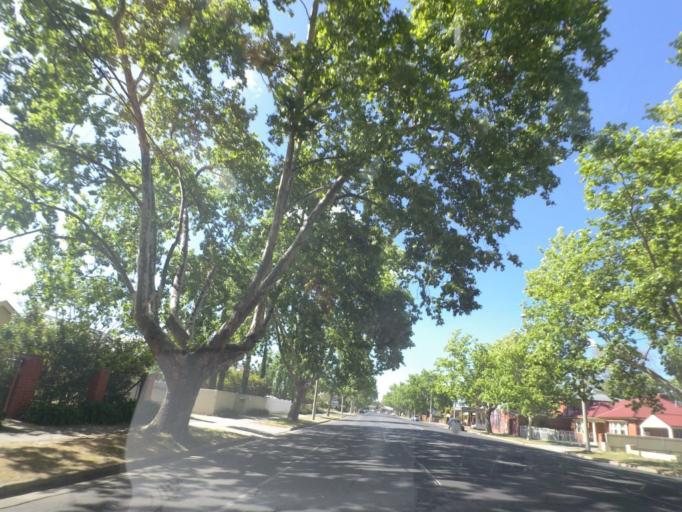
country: AU
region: New South Wales
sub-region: Albury Municipality
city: Albury
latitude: -36.0709
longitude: 146.9261
